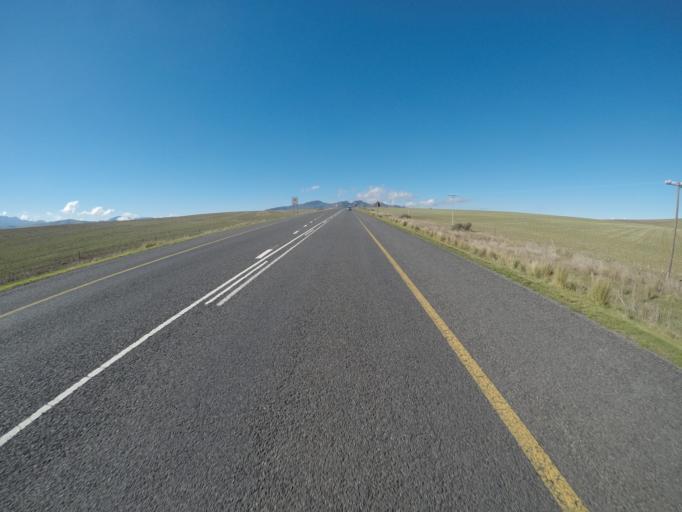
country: ZA
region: Western Cape
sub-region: Overberg District Municipality
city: Caledon
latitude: -34.2107
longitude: 19.3755
